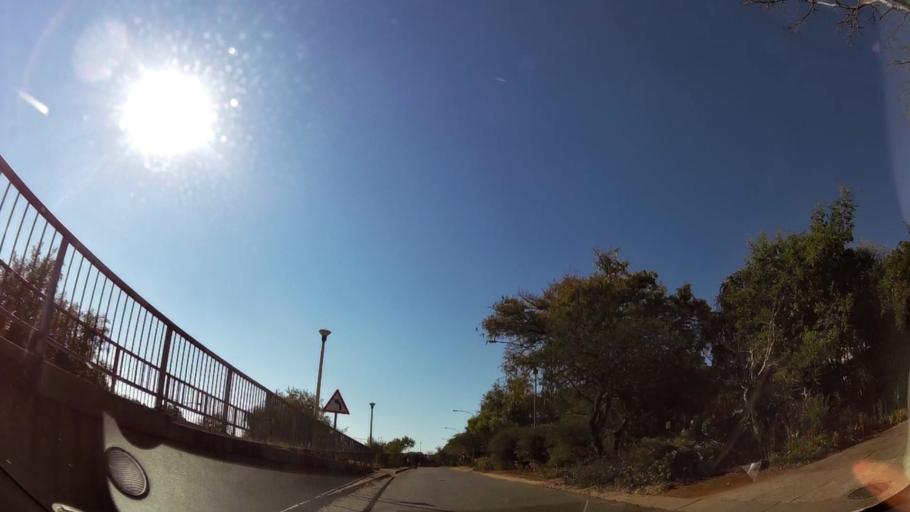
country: ZA
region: Gauteng
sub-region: City of Tshwane Metropolitan Municipality
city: Centurion
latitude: -25.8166
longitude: 28.2075
